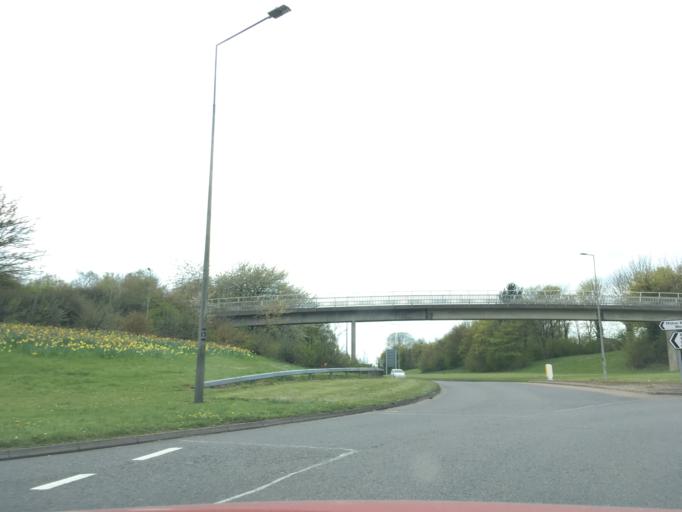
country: GB
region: England
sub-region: Milton Keynes
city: Milton Keynes
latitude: 52.0312
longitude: -0.7455
